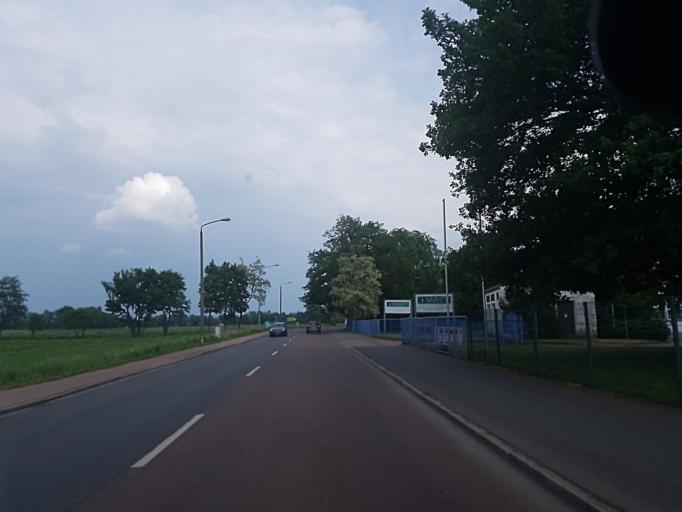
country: DE
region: Saxony-Anhalt
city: Wittenburg
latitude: 51.8748
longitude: 12.6128
